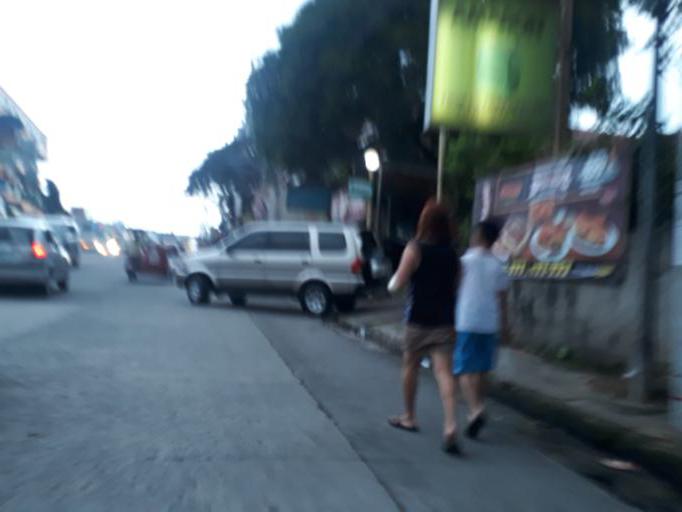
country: PH
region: Metro Manila
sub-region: Quezon City
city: Quezon City
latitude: 14.6837
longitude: 121.0780
